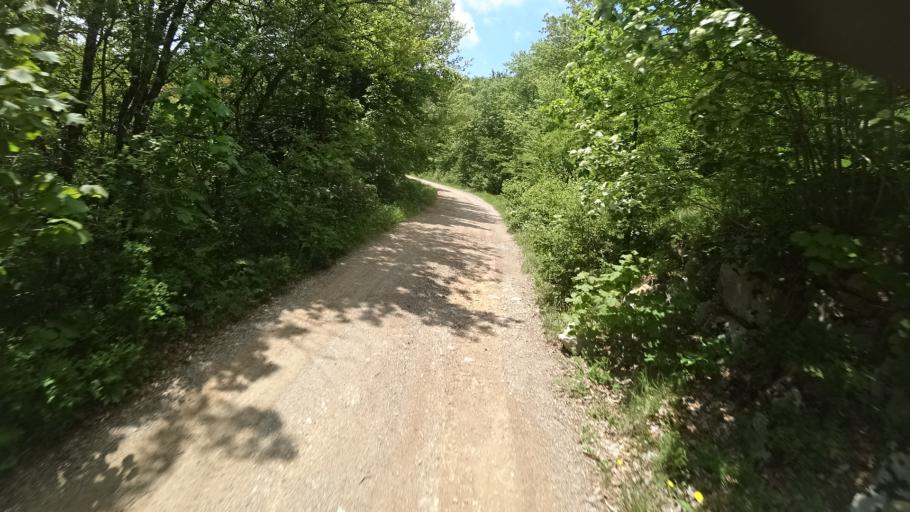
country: HR
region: Zadarska
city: Gracac
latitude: 44.5008
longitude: 15.8782
